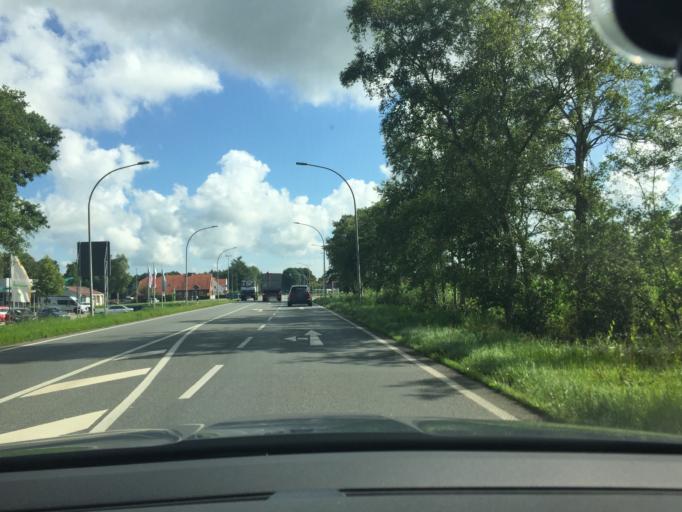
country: DE
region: Lower Saxony
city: Blomberg
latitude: 53.5363
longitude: 7.5940
